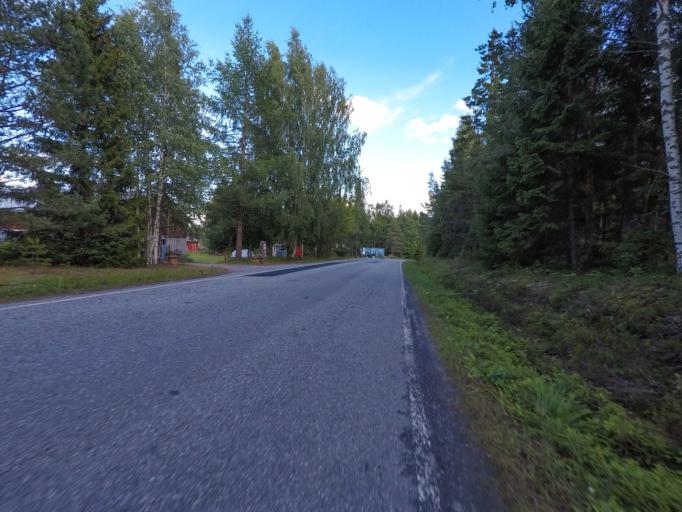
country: FI
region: South Karelia
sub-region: Lappeenranta
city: Joutseno
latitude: 61.1438
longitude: 28.6291
